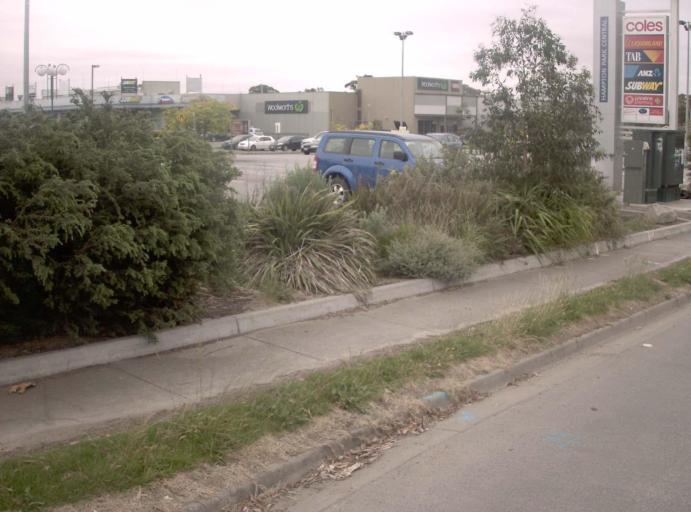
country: AU
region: Victoria
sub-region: Casey
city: Hallam
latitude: -38.0340
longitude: 145.2675
